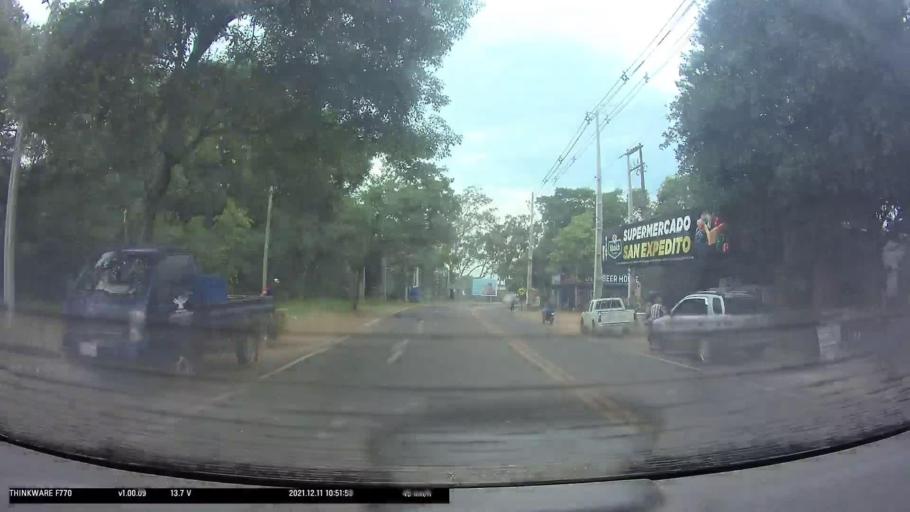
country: PY
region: Cordillera
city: San Bernardino
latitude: -25.2959
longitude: -57.2689
